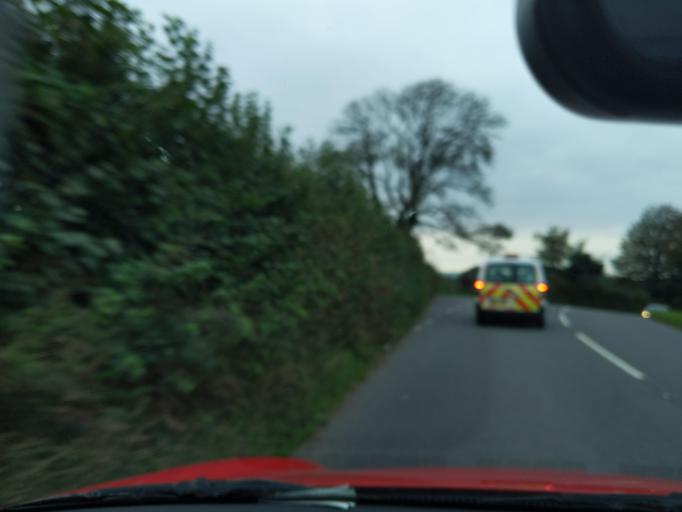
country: GB
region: England
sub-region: Devon
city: Great Torrington
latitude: 50.8661
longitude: -4.0703
